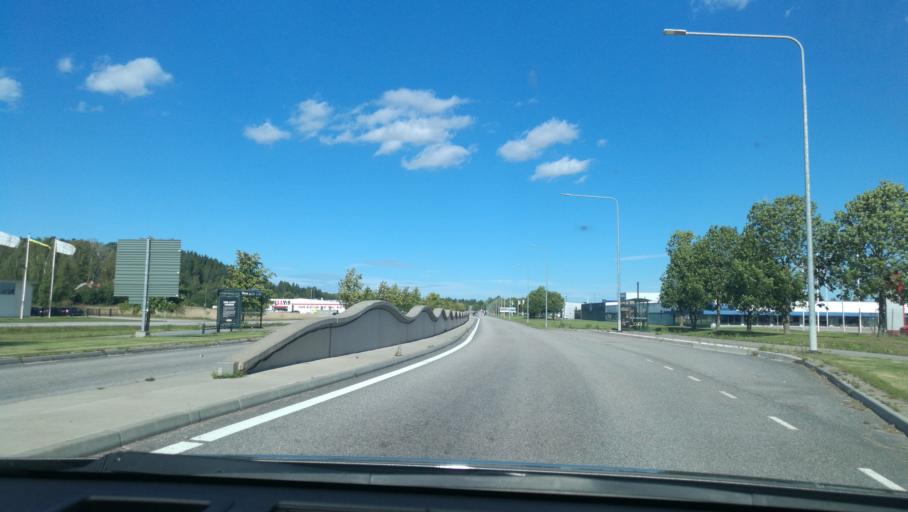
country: SE
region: Vaestra Goetaland
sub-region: Mariestads Kommun
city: Mariestad
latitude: 58.6791
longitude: 13.8170
